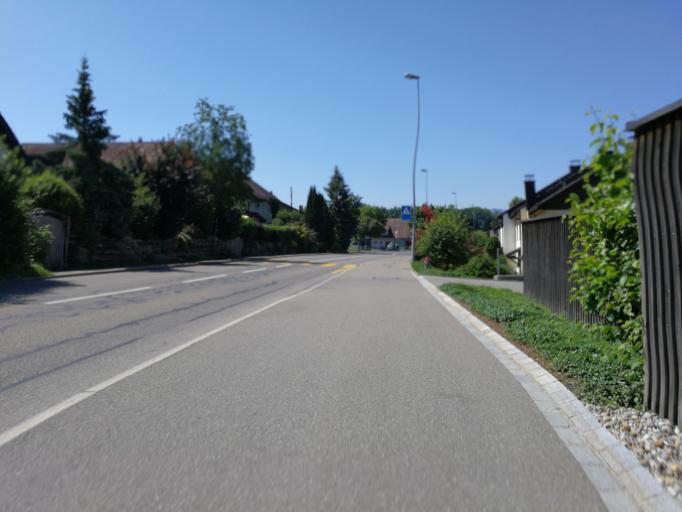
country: CH
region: Zurich
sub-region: Bezirk Hinwil
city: Bubikon
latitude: 47.2652
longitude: 8.8153
